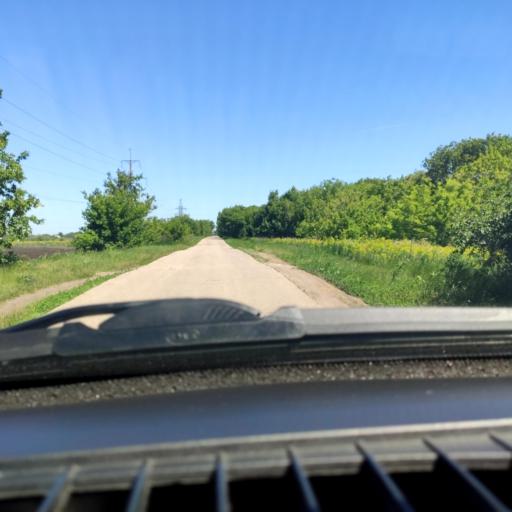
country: RU
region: Samara
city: Tol'yatti
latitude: 53.5867
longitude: 49.4289
